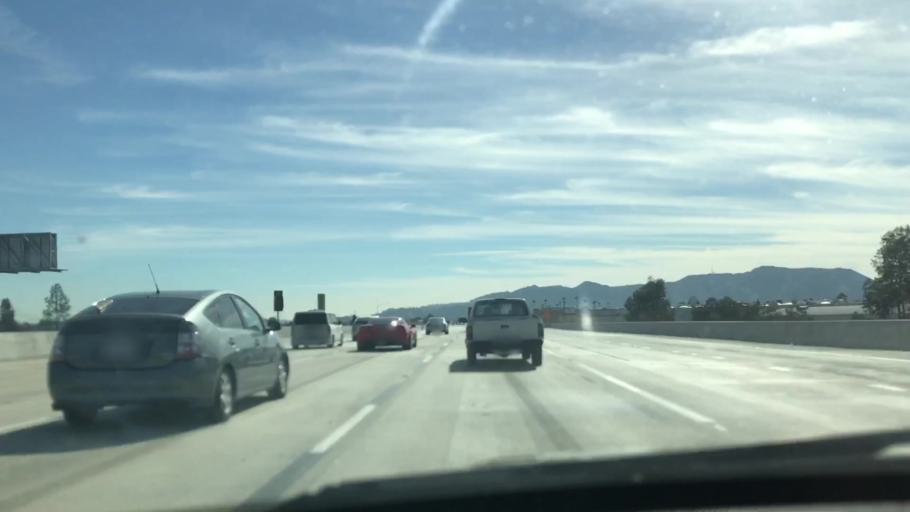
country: US
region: California
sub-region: Los Angeles County
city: Burbank
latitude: 34.2062
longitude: -118.3443
